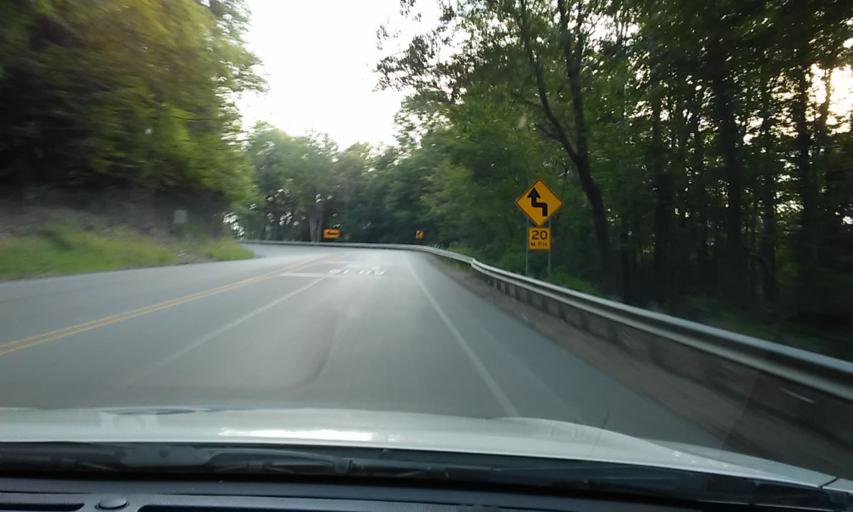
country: US
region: Pennsylvania
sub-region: McKean County
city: Kane
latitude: 41.6250
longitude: -78.8280
